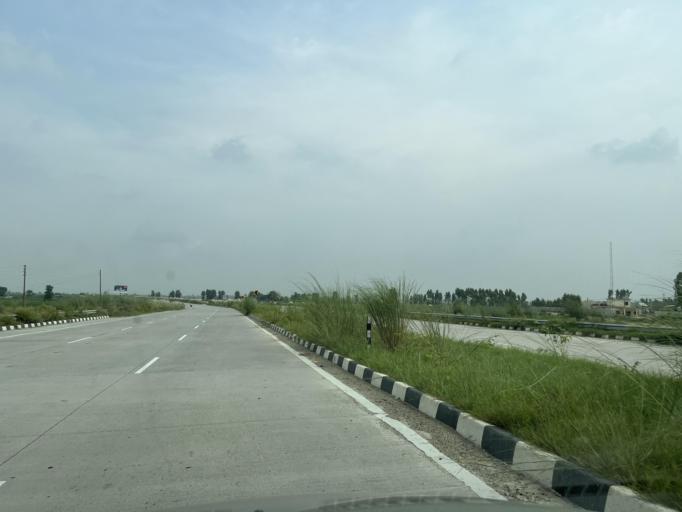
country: IN
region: Uttarakhand
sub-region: Udham Singh Nagar
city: Bazpur
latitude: 29.1494
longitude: 79.0247
